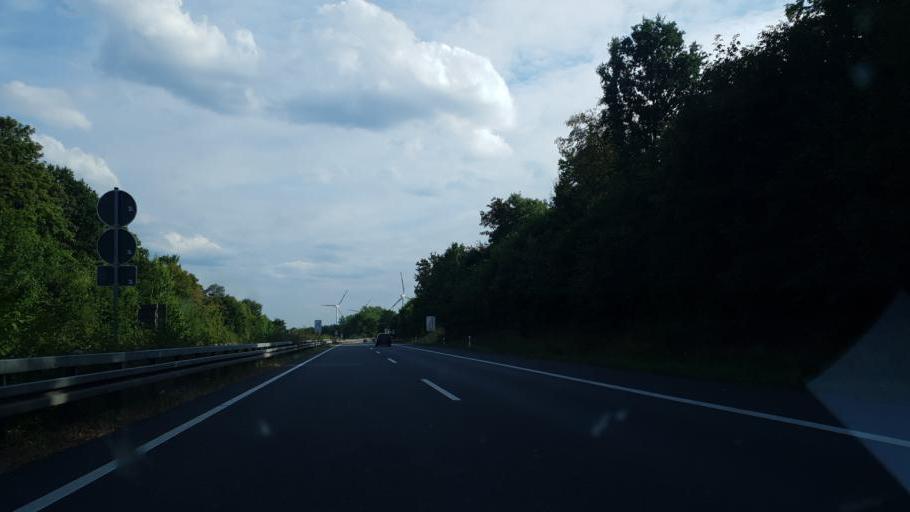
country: DE
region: Lower Saxony
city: Holle
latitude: 52.0936
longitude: 10.1822
